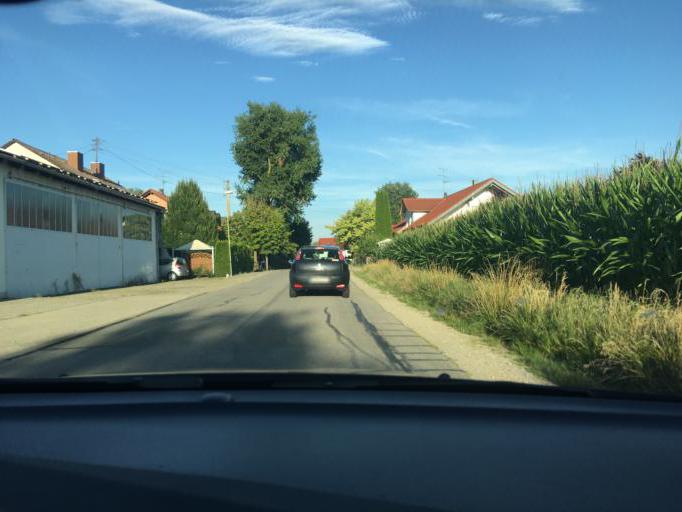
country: DE
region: Bavaria
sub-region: Upper Bavaria
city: Bockhorn
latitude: 48.2896
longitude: 11.9954
